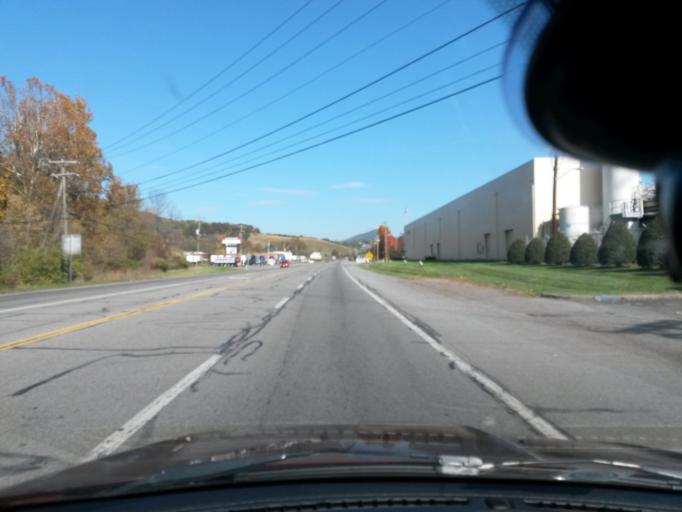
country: US
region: Virginia
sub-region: Roanoke County
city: Hollins
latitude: 37.3575
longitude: -79.9275
